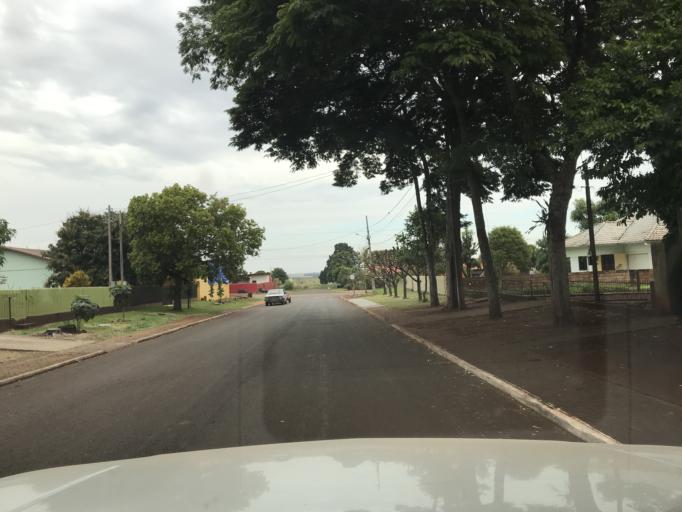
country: BR
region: Parana
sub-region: Marechal Candido Rondon
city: Marechal Candido Rondon
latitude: -24.4681
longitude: -53.9586
